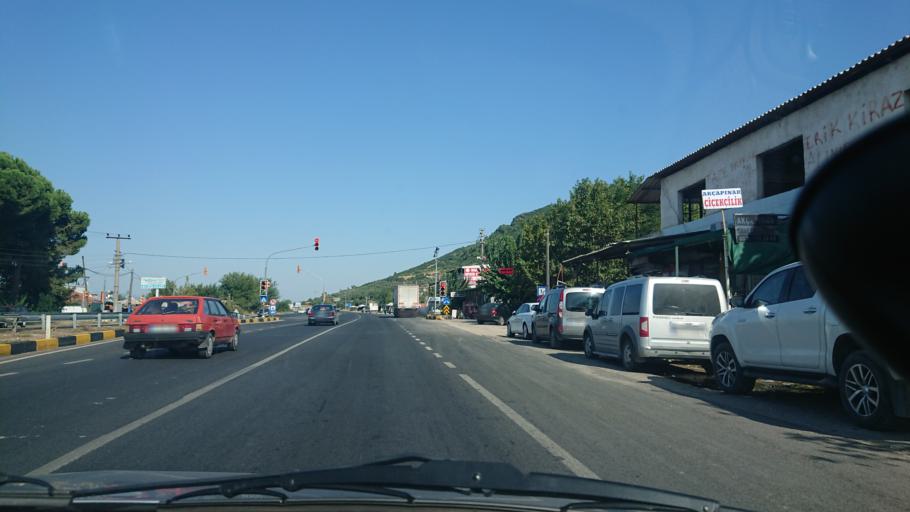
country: TR
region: Manisa
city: Ahmetli
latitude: 38.4901
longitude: 27.8411
